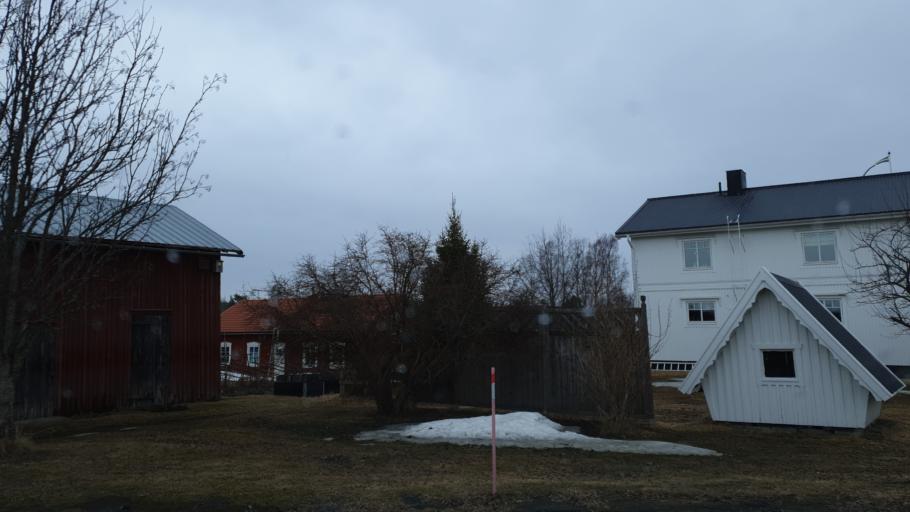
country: SE
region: Vaesterbotten
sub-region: Skelleftea Kommun
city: Kage
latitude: 64.8341
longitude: 20.9967
